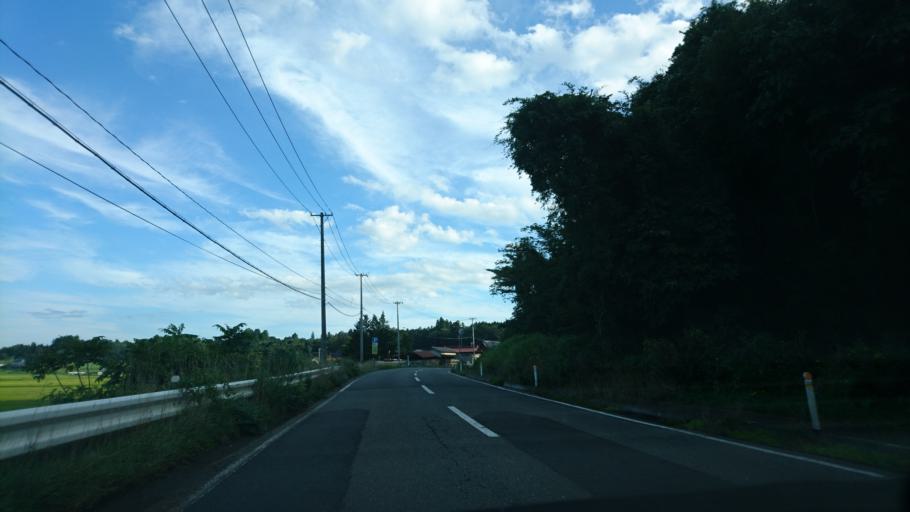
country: JP
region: Iwate
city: Ichinoseki
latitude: 38.8694
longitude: 141.1965
